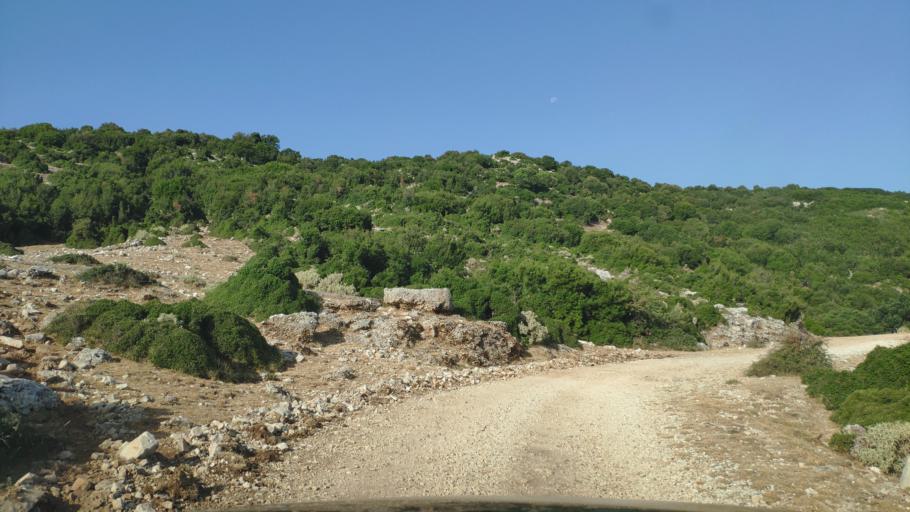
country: GR
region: West Greece
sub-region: Nomos Aitolias kai Akarnanias
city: Monastirakion
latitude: 38.8345
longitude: 20.9832
